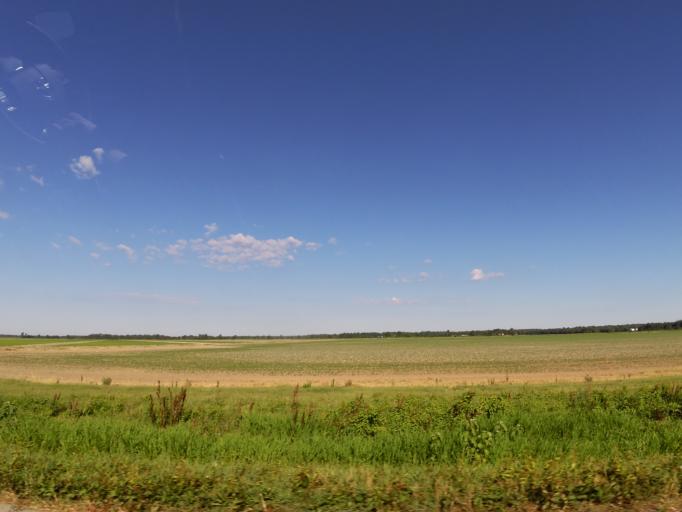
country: US
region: Missouri
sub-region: Butler County
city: Poplar Bluff
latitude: 36.6318
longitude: -90.5203
